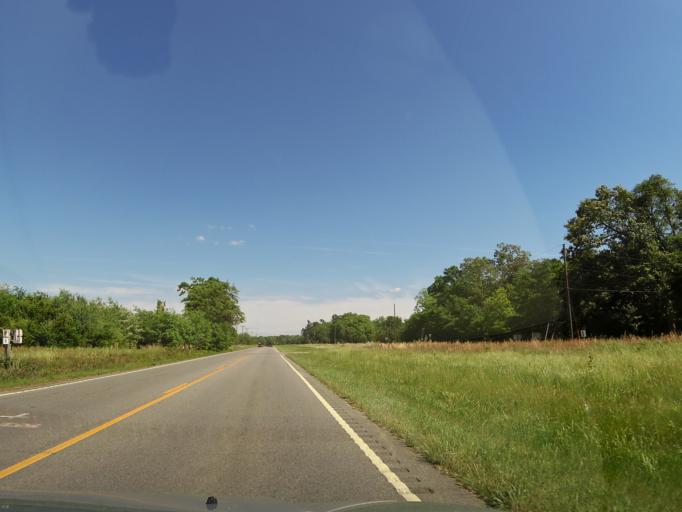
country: US
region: South Carolina
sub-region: Aiken County
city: Aiken
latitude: 33.5329
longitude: -81.6443
